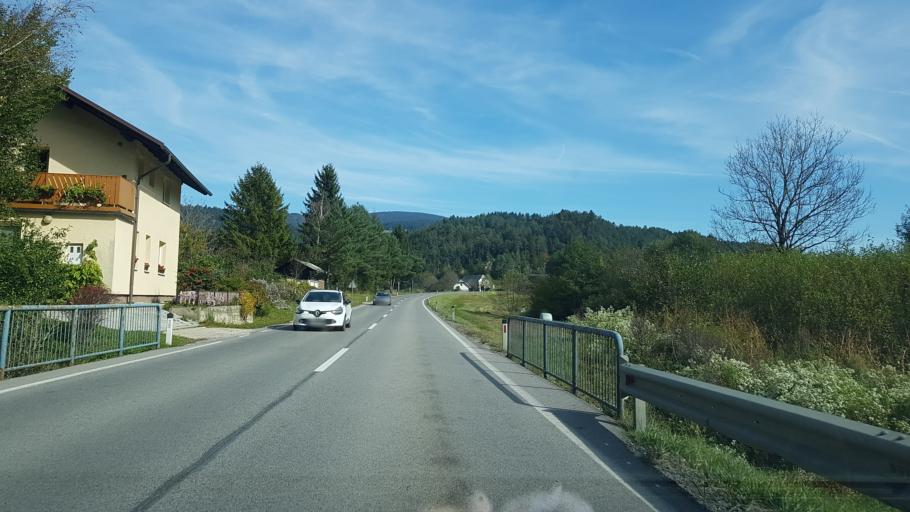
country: SI
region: Mislinja
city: Mislinja
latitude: 46.4233
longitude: 15.1823
